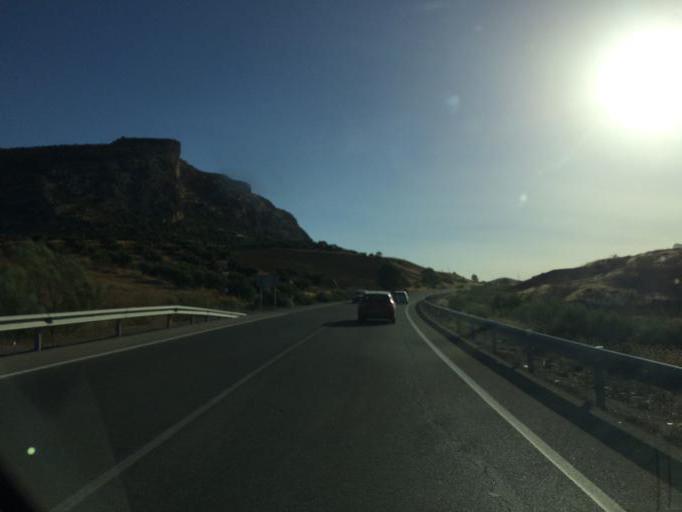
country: ES
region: Andalusia
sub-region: Provincia de Malaga
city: Teba
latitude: 36.9621
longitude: -4.8561
